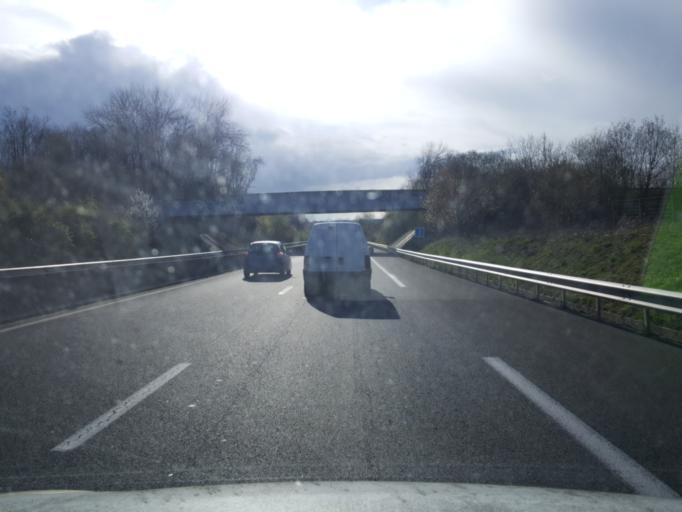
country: FR
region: Picardie
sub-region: Departement de l'Oise
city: Goincourt
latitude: 49.3850
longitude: 2.0566
